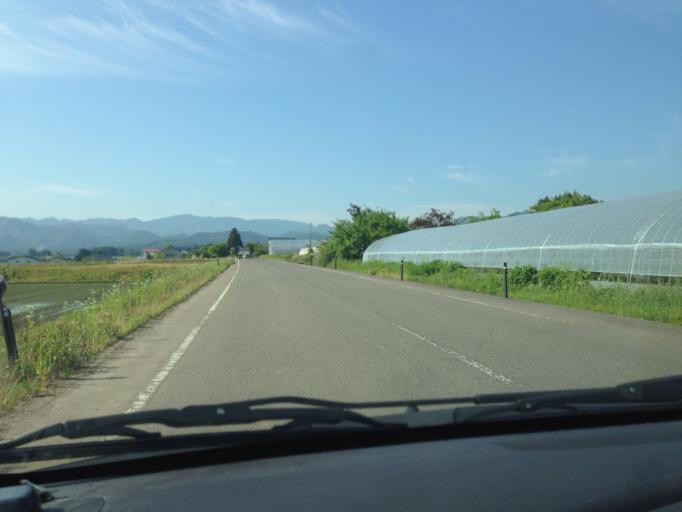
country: JP
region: Fukushima
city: Kitakata
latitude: 37.4653
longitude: 139.8163
